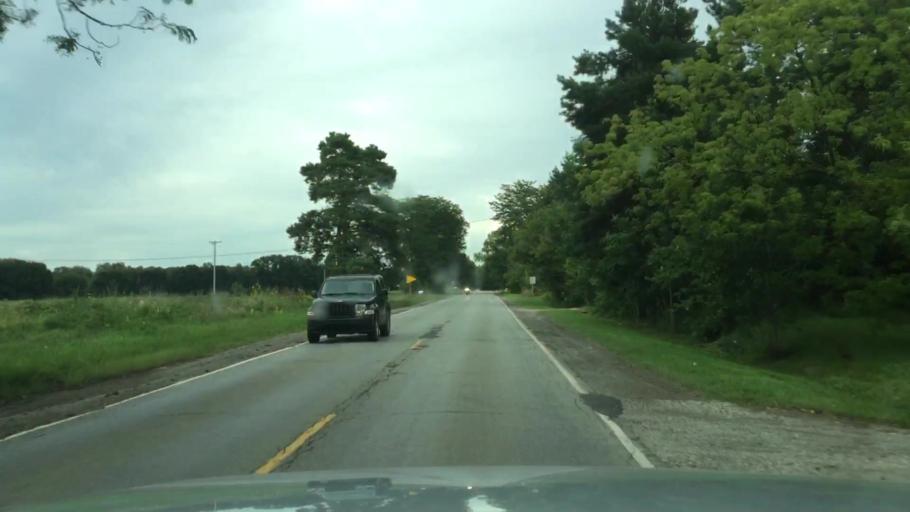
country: US
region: Michigan
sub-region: Genesee County
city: Argentine
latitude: 42.8030
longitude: -83.8721
